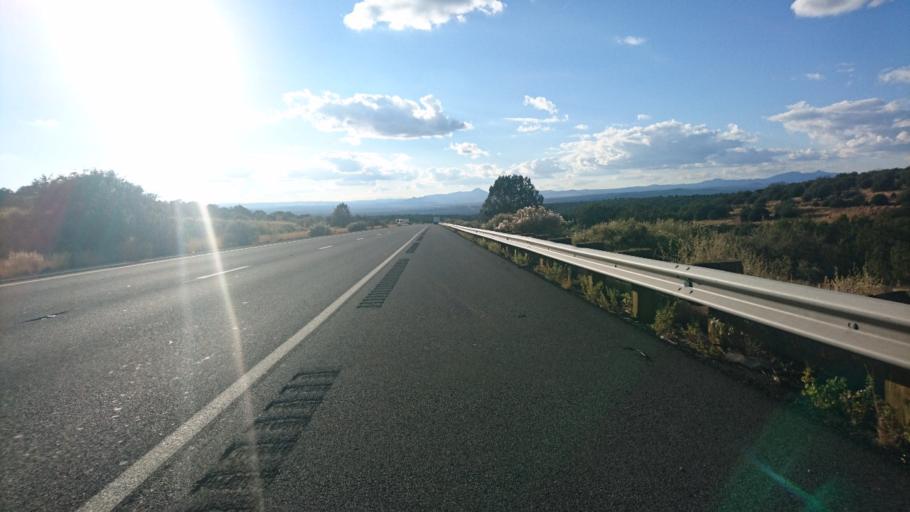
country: US
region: Arizona
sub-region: Coconino County
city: Williams
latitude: 35.2161
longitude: -112.3853
